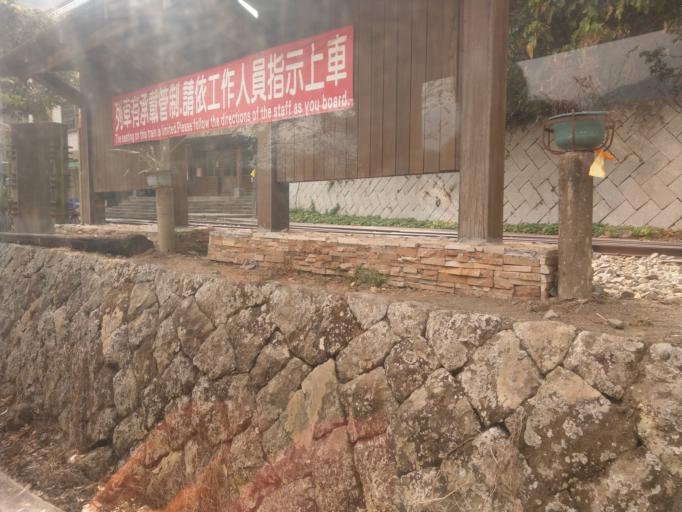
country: TW
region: Taiwan
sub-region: Chiayi
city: Jiayi Shi
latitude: 23.5331
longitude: 120.6028
